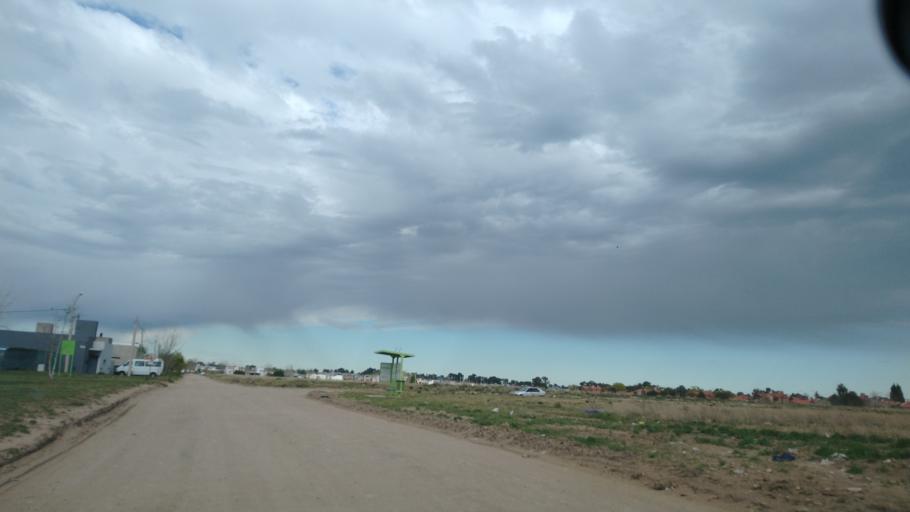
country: AR
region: Buenos Aires
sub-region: Partido de Bahia Blanca
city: Bahia Blanca
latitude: -38.7052
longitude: -62.2078
